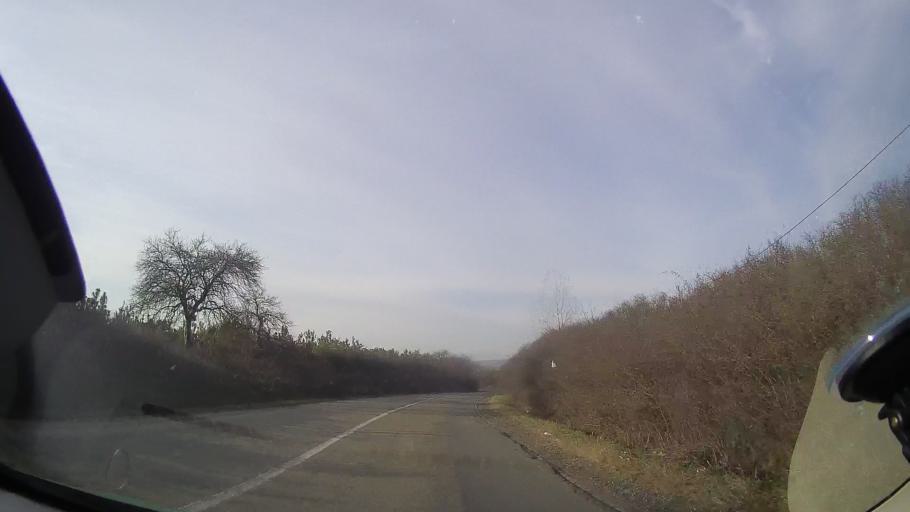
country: RO
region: Bihor
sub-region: Comuna Ciuhoiu
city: Ciuhoiu
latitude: 47.2260
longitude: 22.1554
